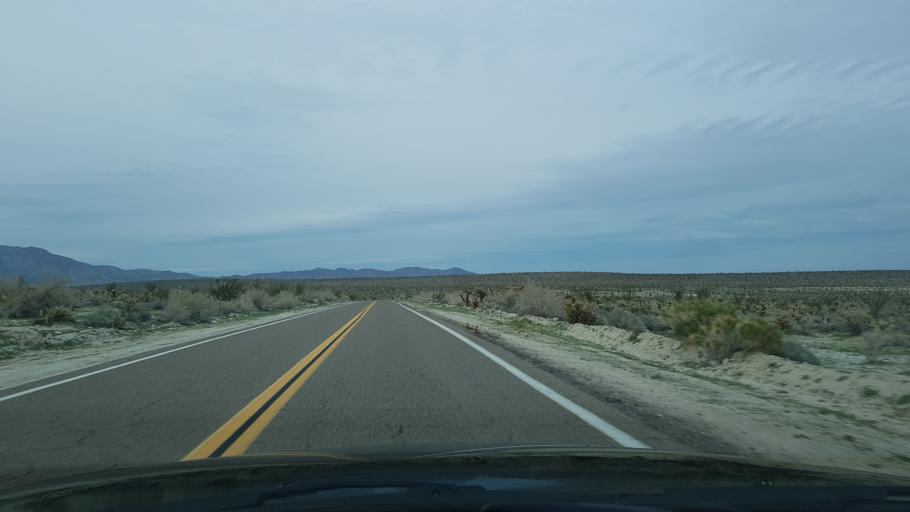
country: US
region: California
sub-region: San Diego County
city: Pine Valley
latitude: 32.8732
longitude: -116.2092
